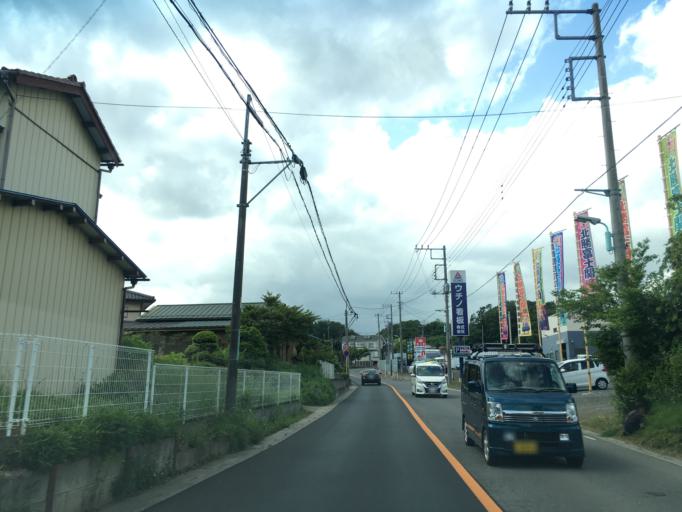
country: JP
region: Saitama
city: Tokorozawa
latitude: 35.7873
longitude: 139.4165
